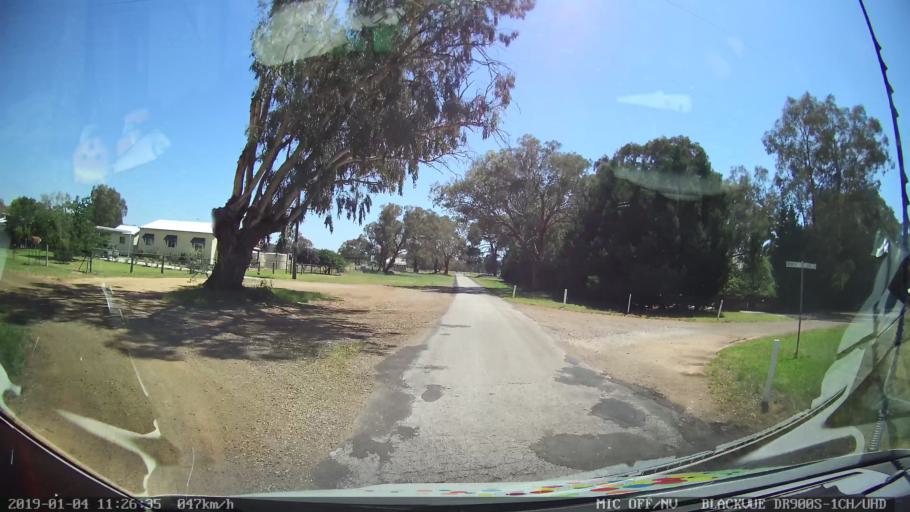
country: AU
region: New South Wales
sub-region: Cabonne
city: Molong
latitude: -33.1144
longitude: 148.7565
